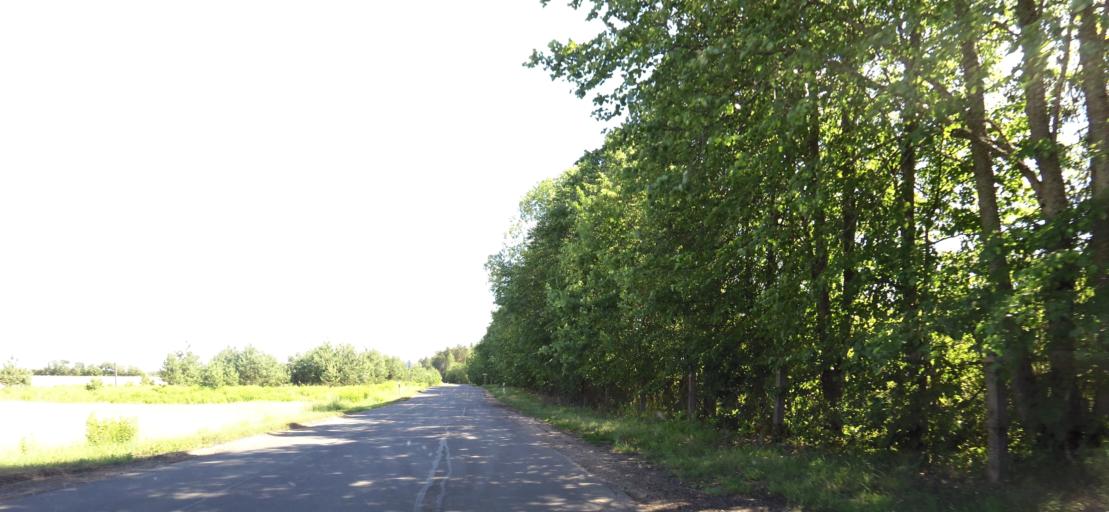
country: LT
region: Vilnius County
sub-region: Vilnius
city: Fabijoniskes
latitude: 54.8054
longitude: 25.3280
